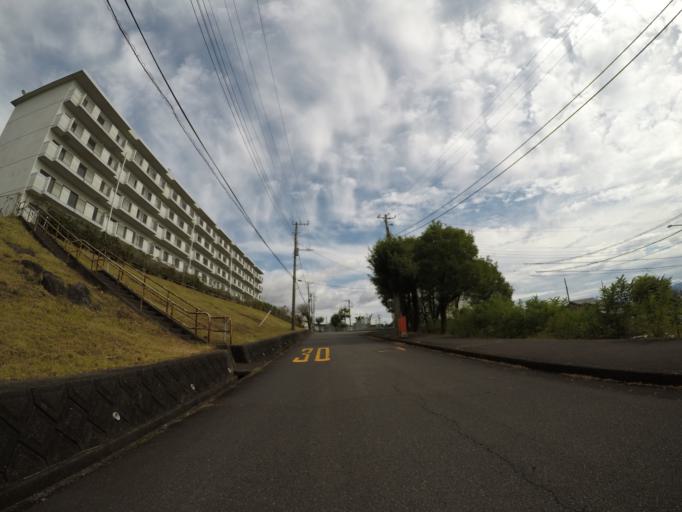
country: JP
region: Shizuoka
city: Fuji
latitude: 35.1826
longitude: 138.7175
